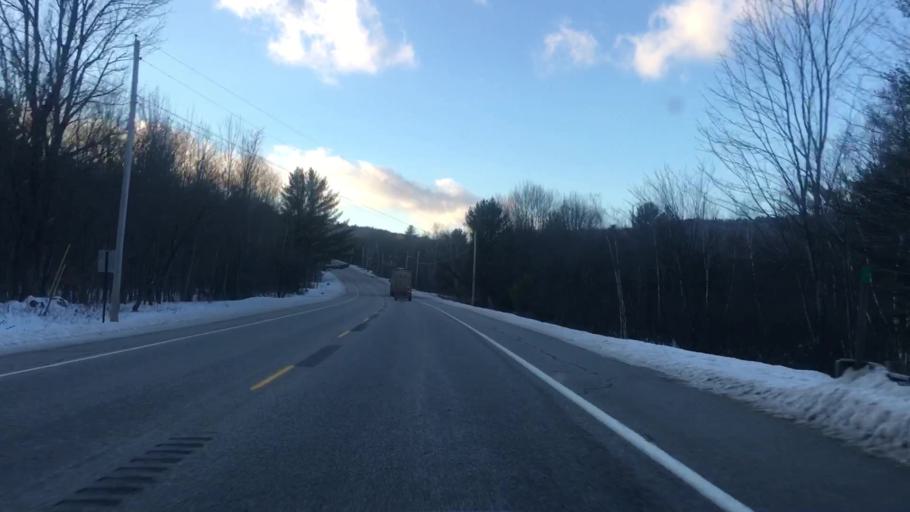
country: US
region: Maine
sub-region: Oxford County
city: Peru
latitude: 44.5871
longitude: -70.3470
